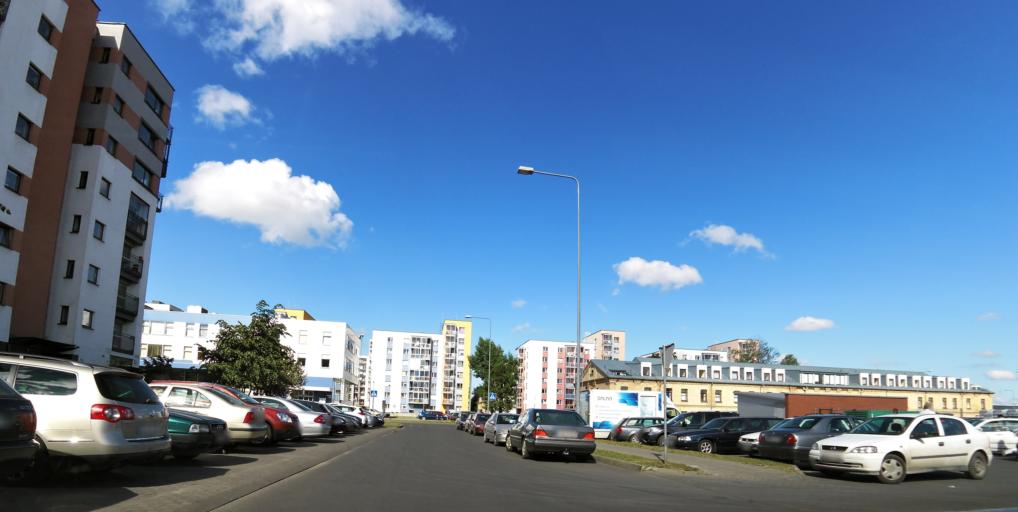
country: LT
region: Vilnius County
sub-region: Vilnius
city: Vilnius
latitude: 54.7091
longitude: 25.2987
